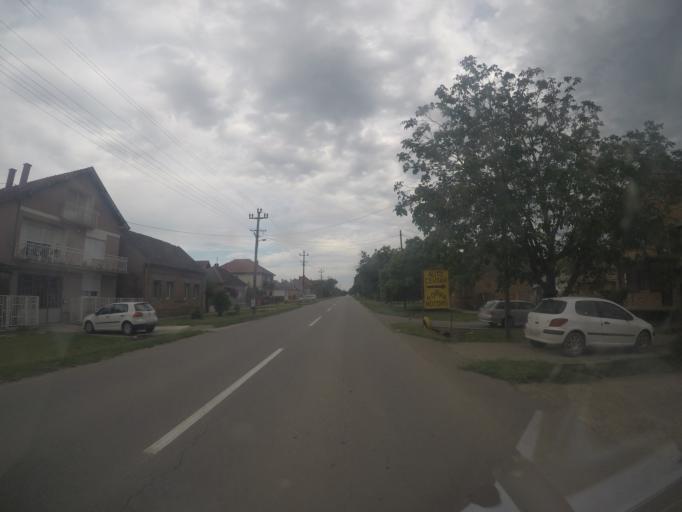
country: RS
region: Autonomna Pokrajina Vojvodina
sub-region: Juznobanatski Okrug
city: Opovo
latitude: 45.0435
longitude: 20.4406
